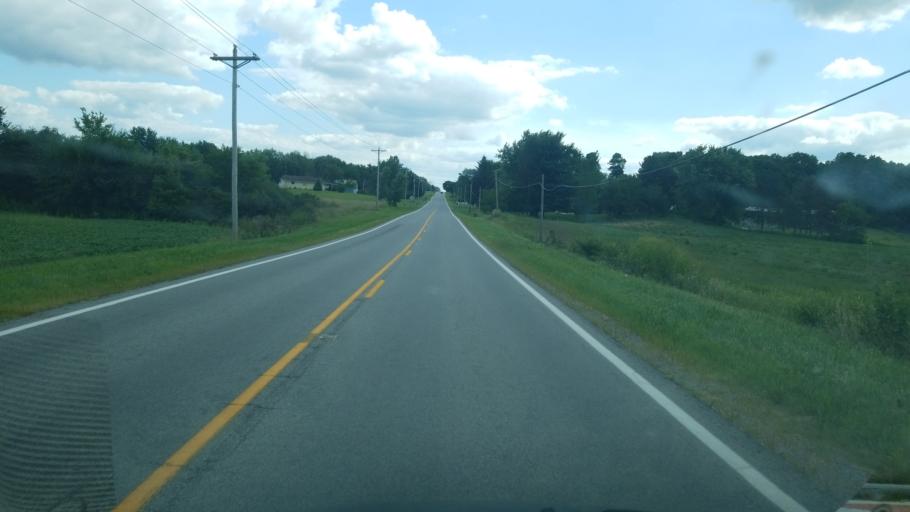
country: US
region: Ohio
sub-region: Allen County
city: Lima
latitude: 40.6506
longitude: -83.9756
